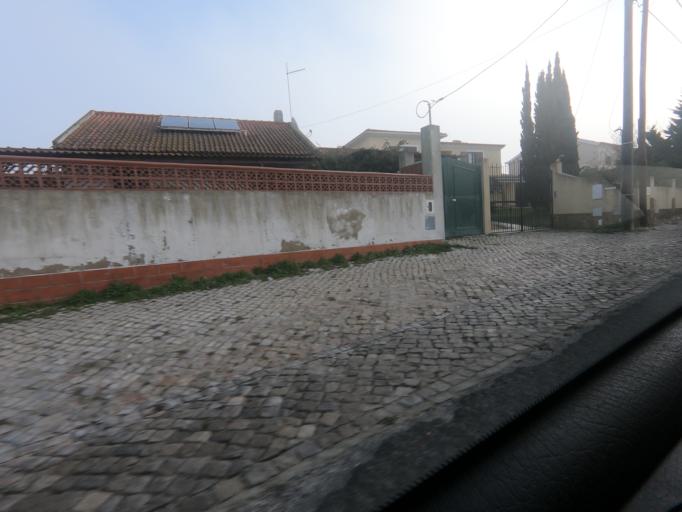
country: PT
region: Setubal
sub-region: Palmela
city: Palmela
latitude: 38.6011
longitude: -8.9003
